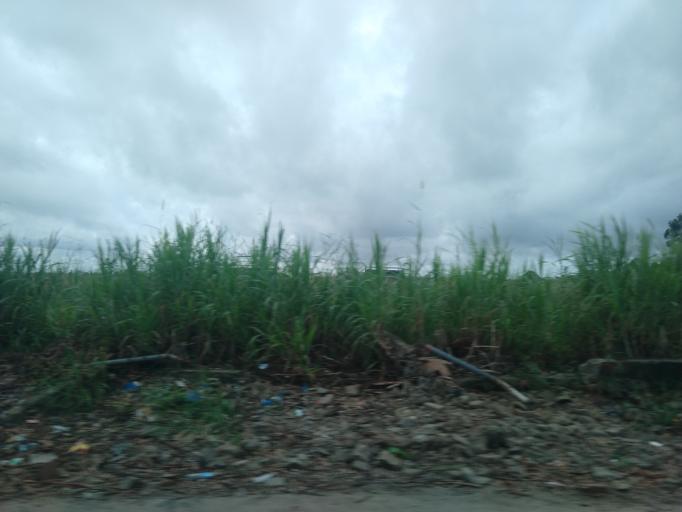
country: MZ
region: Sofala
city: Beira
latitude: -19.7979
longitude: 34.8947
